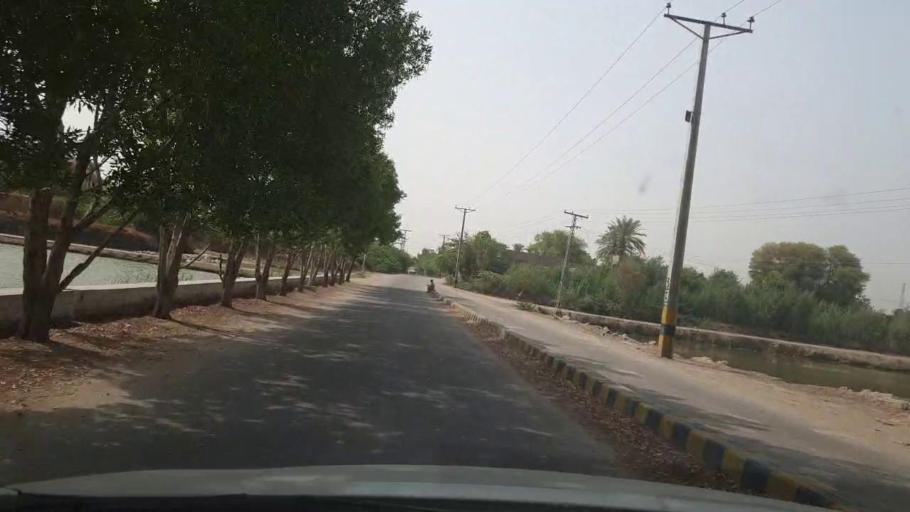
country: PK
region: Sindh
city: Kot Diji
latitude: 27.3503
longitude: 68.7122
